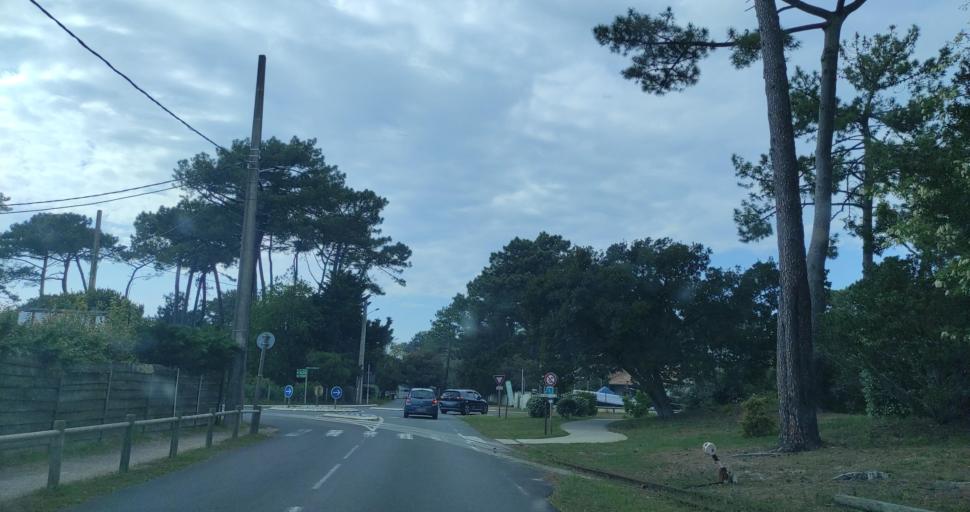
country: FR
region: Aquitaine
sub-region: Departement de la Gironde
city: Arcachon
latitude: 44.6581
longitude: -1.2441
